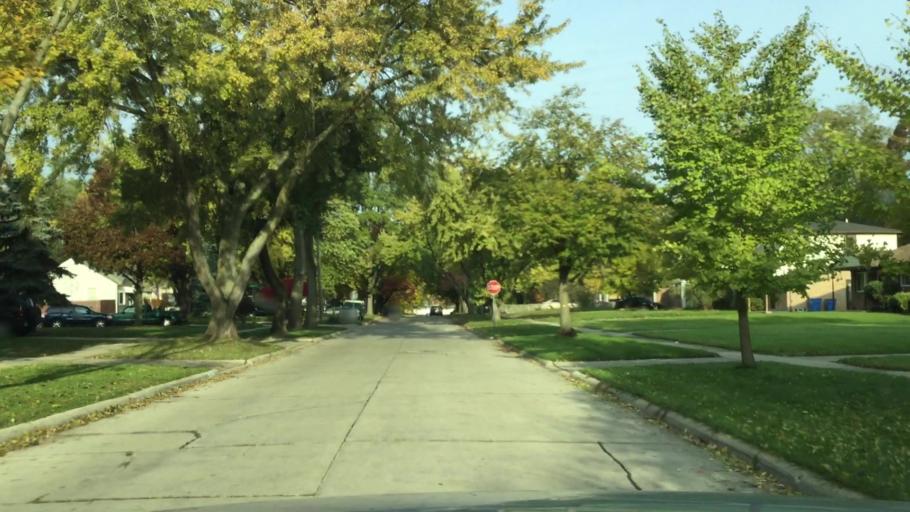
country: US
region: Michigan
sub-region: Wayne County
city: Dearborn Heights
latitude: 42.3546
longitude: -83.2767
